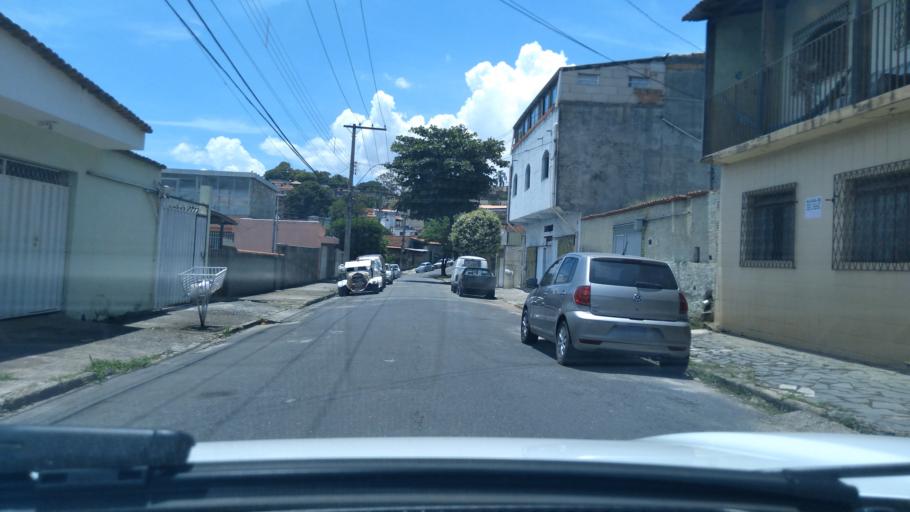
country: BR
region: Minas Gerais
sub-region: Contagem
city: Contagem
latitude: -19.9265
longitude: -44.0114
